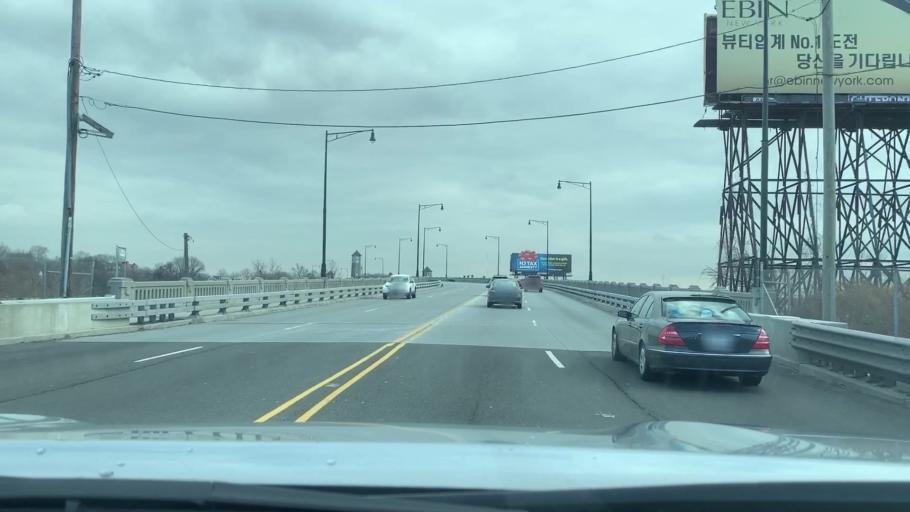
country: US
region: New Jersey
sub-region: Bergen County
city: Little Ferry
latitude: 40.8523
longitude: -74.0323
